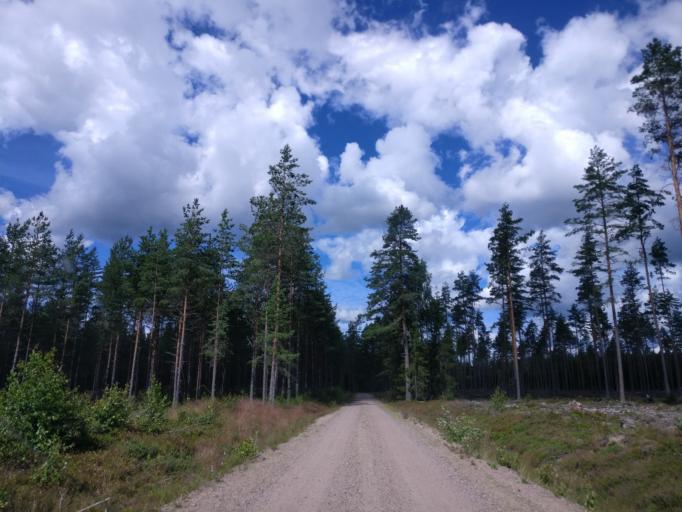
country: SE
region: Vaermland
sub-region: Hagfors Kommun
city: Hagfors
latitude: 60.0302
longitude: 13.5443
